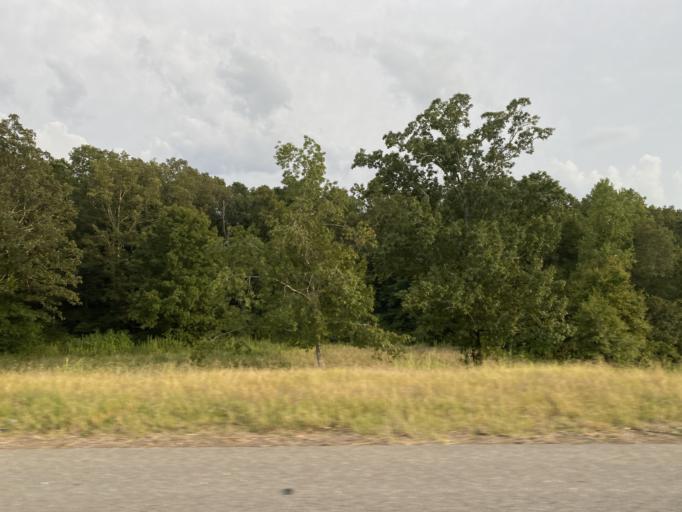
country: US
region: Alabama
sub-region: Franklin County
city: Red Bay
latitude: 34.4492
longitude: -88.0630
